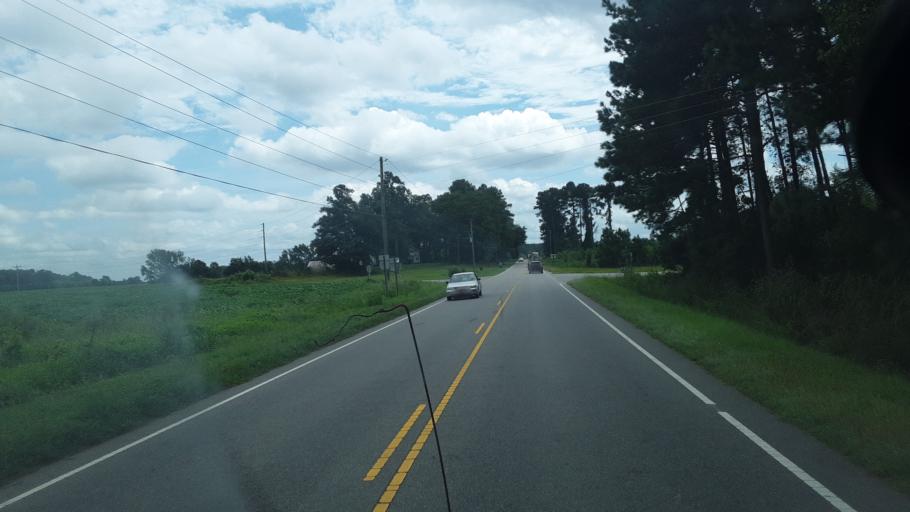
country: US
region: North Carolina
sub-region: Robeson County
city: Rowland
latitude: 34.5020
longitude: -79.2594
